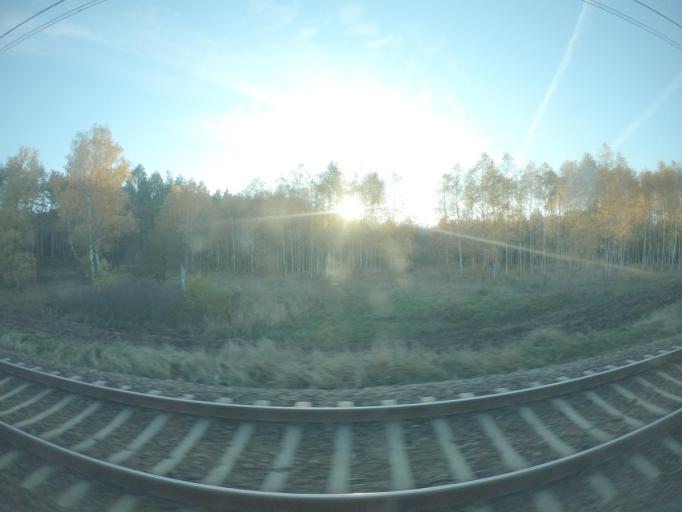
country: PL
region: Lubusz
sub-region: Powiat slubicki
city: Rzepin
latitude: 52.2850
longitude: 14.8975
